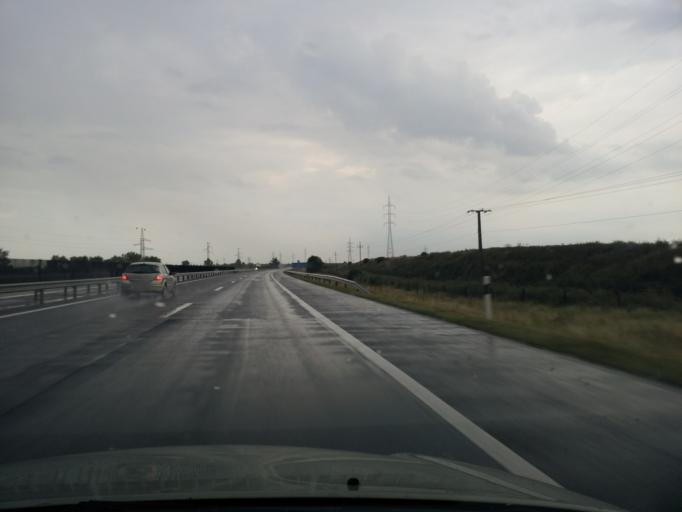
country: HU
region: Borsod-Abauj-Zemplen
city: Onod
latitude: 47.9892
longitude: 20.8953
